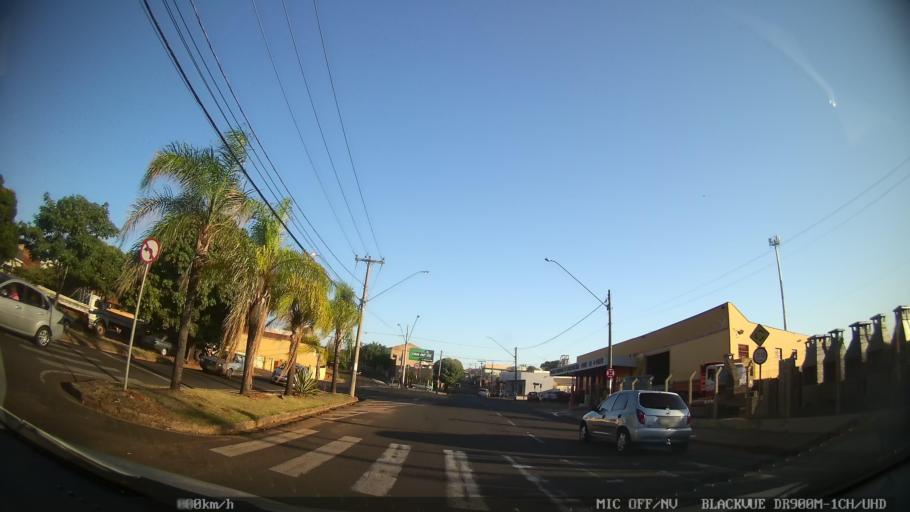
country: BR
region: Sao Paulo
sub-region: Sao Jose Do Rio Preto
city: Sao Jose do Rio Preto
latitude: -20.7872
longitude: -49.3686
